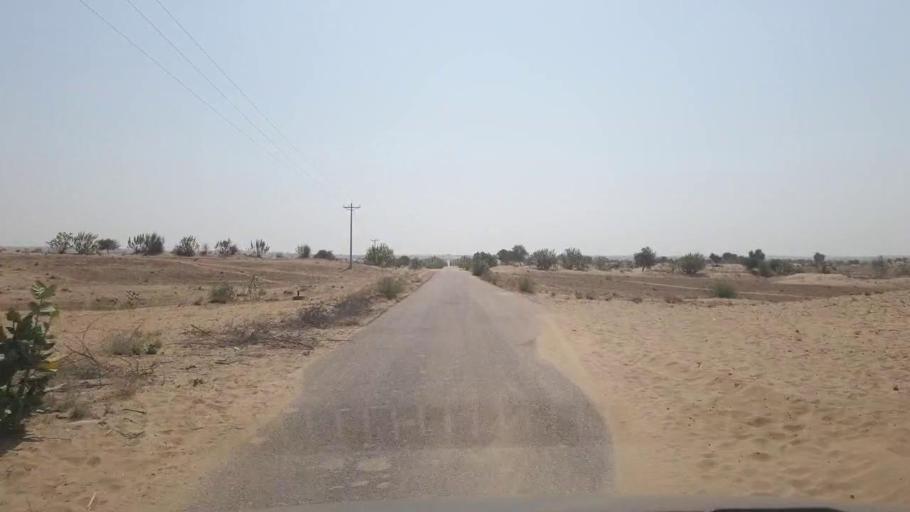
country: PK
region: Sindh
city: Chor
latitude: 25.6062
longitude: 70.1792
